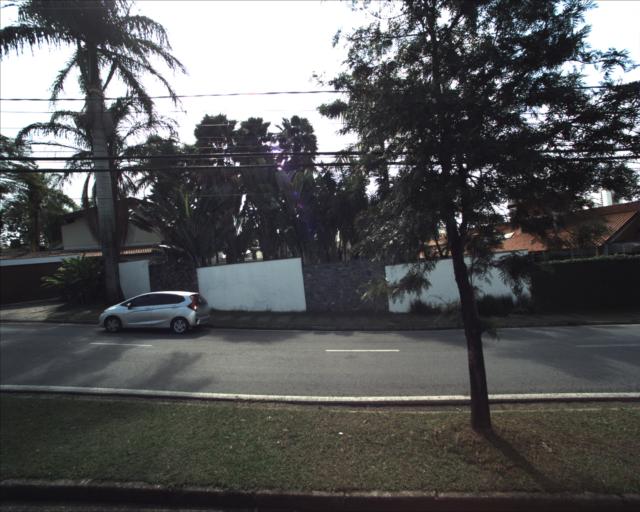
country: BR
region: Sao Paulo
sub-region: Sorocaba
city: Sorocaba
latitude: -23.5227
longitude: -47.4670
